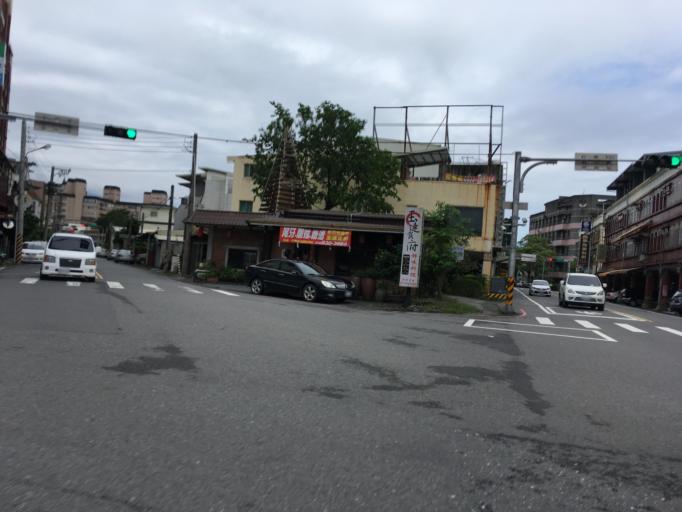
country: TW
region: Taiwan
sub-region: Yilan
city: Yilan
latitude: 24.7425
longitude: 121.7530
